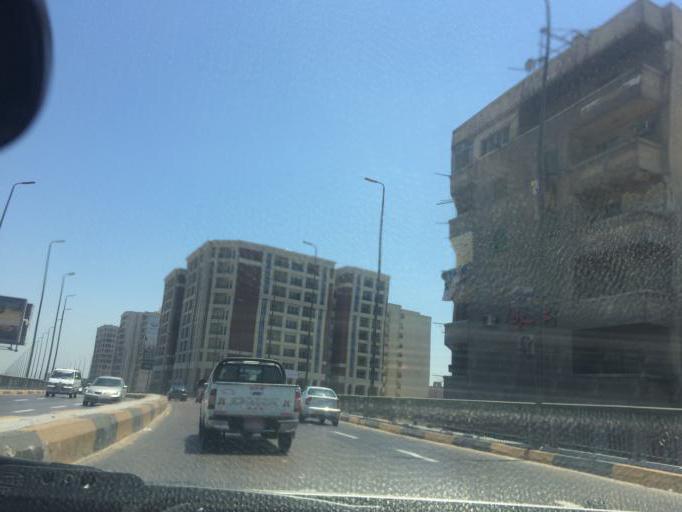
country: EG
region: Alexandria
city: Alexandria
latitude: 31.1899
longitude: 29.9236
